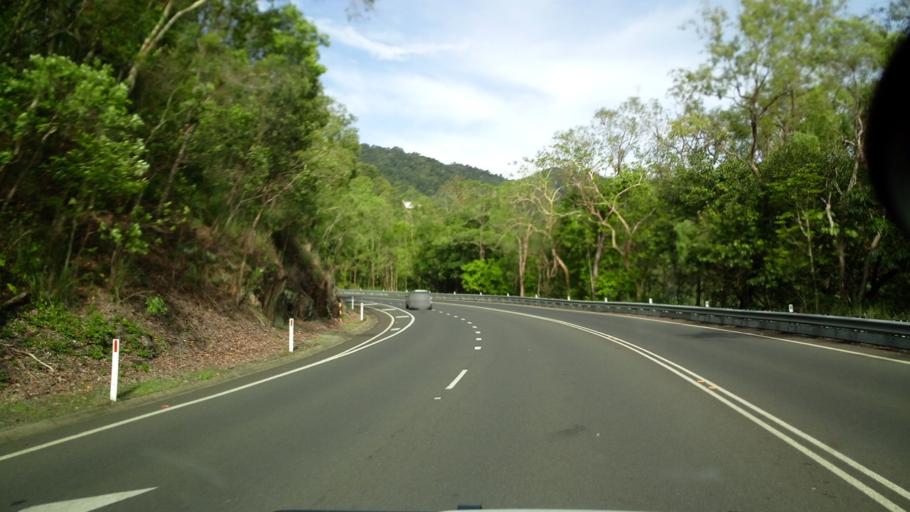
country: AU
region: Queensland
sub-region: Cairns
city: Redlynch
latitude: -16.8372
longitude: 145.6857
